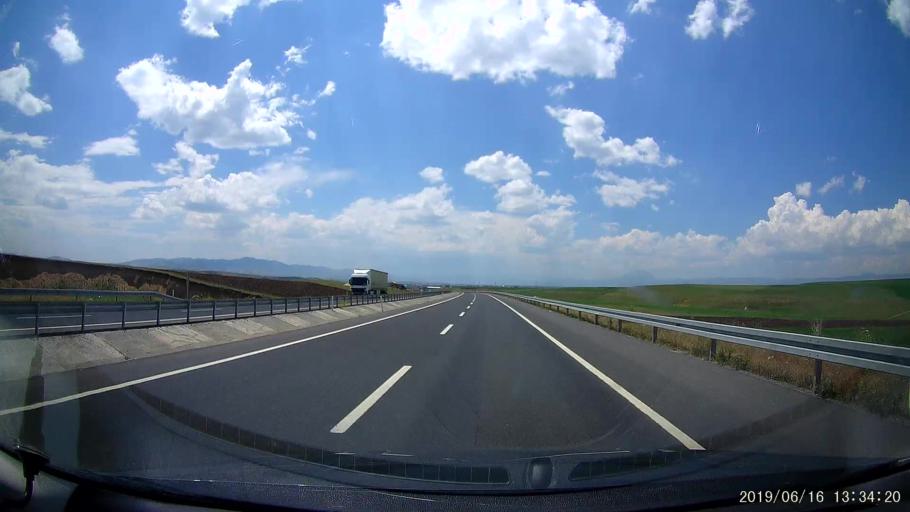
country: TR
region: Agri
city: Agri
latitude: 39.7126
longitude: 43.1292
